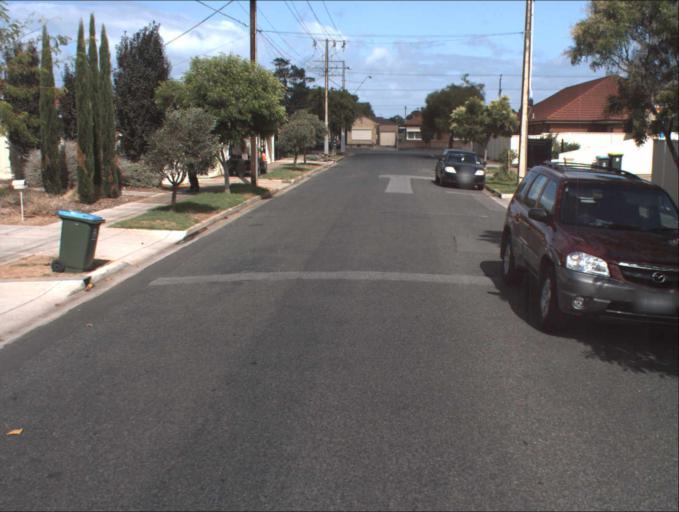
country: AU
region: South Australia
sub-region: Charles Sturt
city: Woodville North
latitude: -34.8705
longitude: 138.5491
